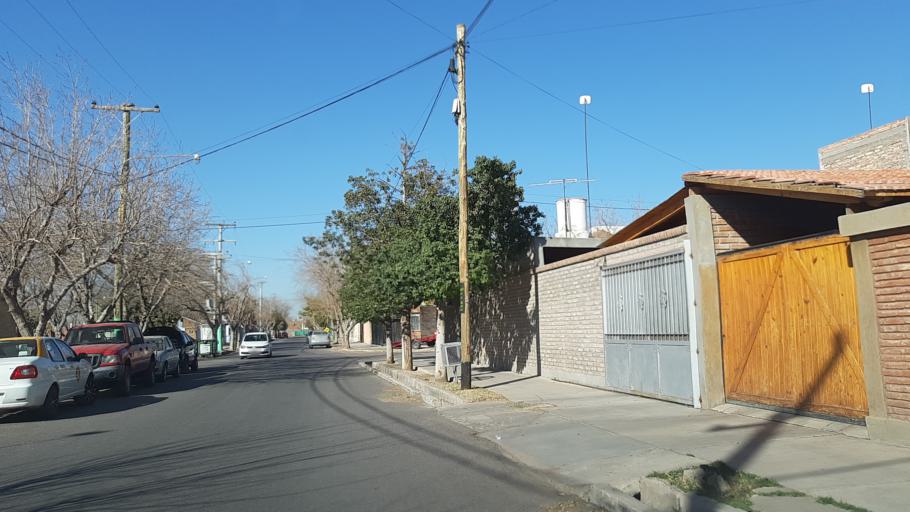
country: AR
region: San Juan
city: Villa Paula de Sarmiento
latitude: -31.5166
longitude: -68.5898
